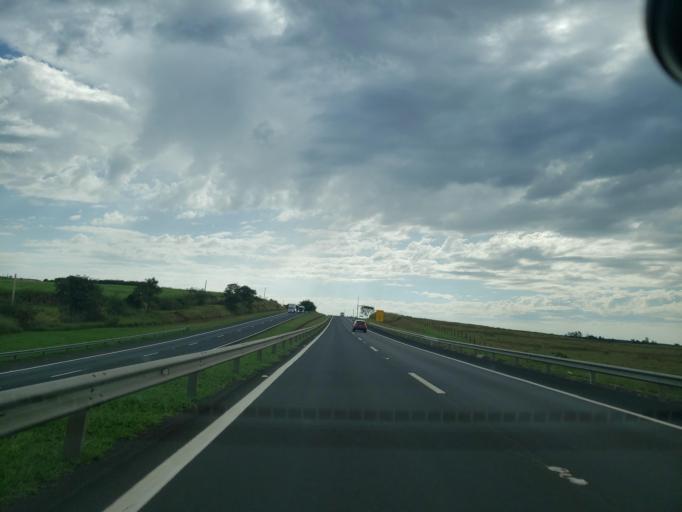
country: BR
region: Sao Paulo
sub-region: Cafelandia
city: Cafelandia
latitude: -21.7781
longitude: -49.6606
